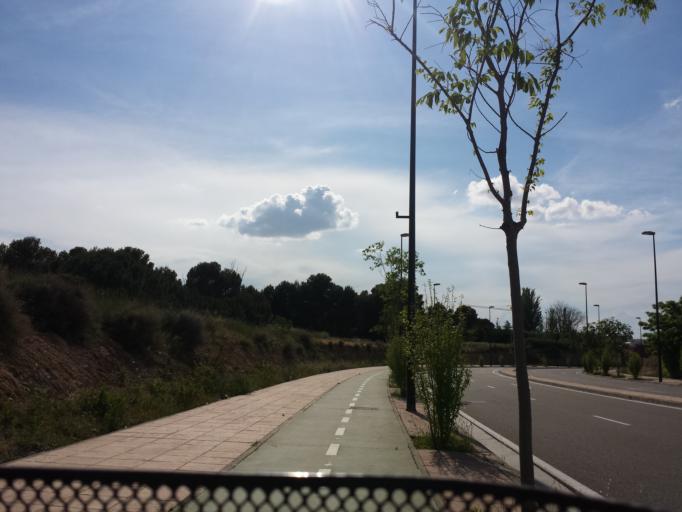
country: ES
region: Aragon
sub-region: Provincia de Zaragoza
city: Montecanal
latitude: 41.6340
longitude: -0.9362
